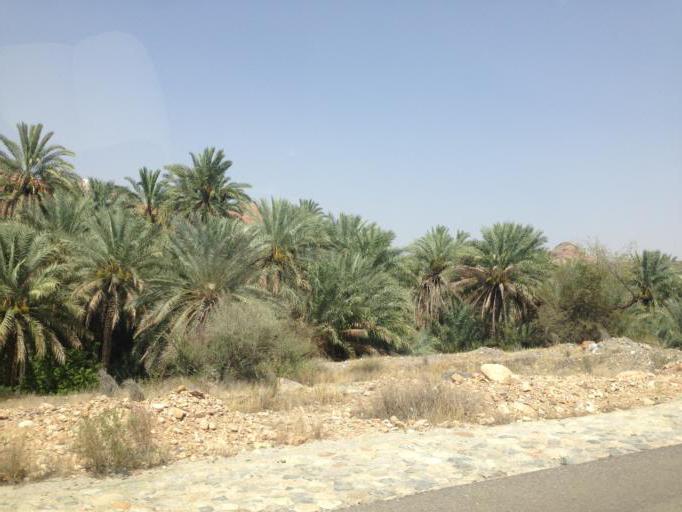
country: OM
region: Ash Sharqiyah
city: Ibra'
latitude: 23.0845
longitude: 58.8647
